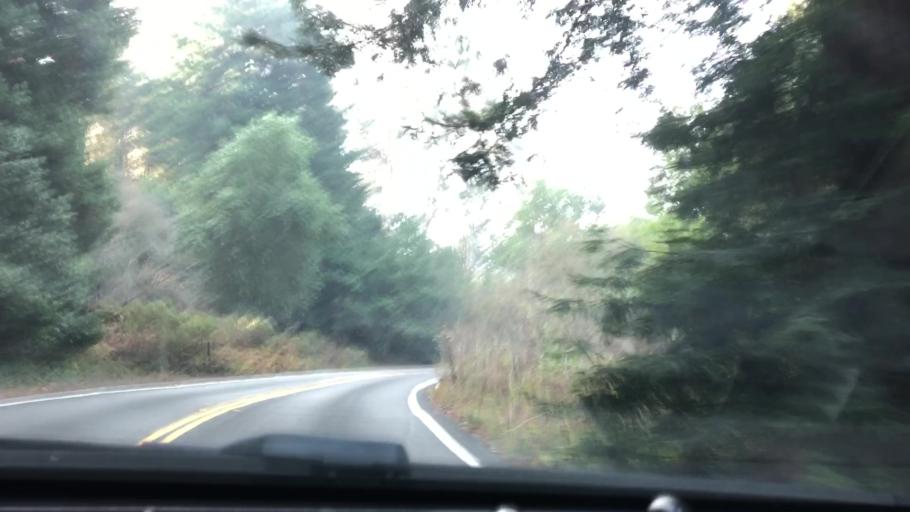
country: US
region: California
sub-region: Alameda County
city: Berkeley
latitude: 37.8849
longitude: -122.2428
